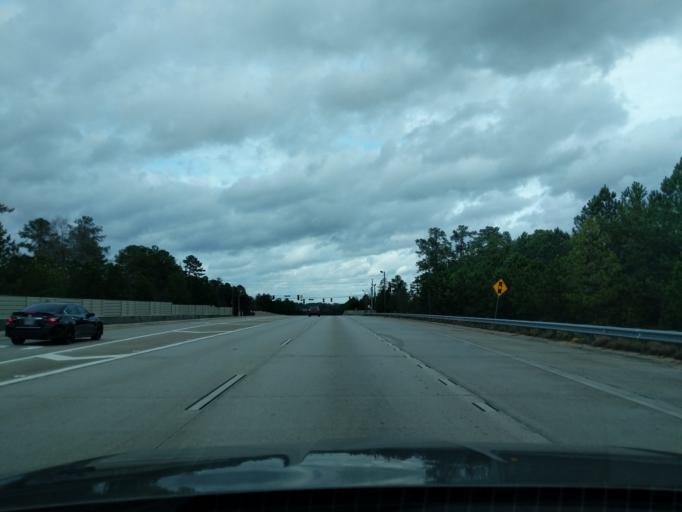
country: US
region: Georgia
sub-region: Columbia County
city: Martinez
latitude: 33.4583
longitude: -82.1190
